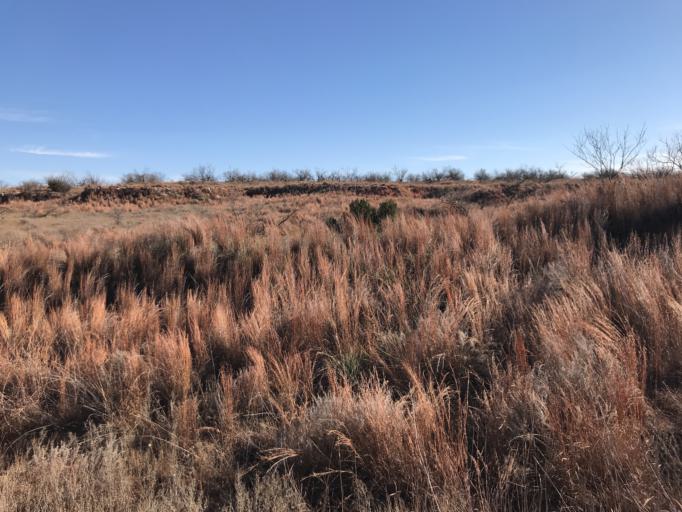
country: US
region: Texas
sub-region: Childress County
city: Childress
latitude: 34.3269
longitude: -100.4743
